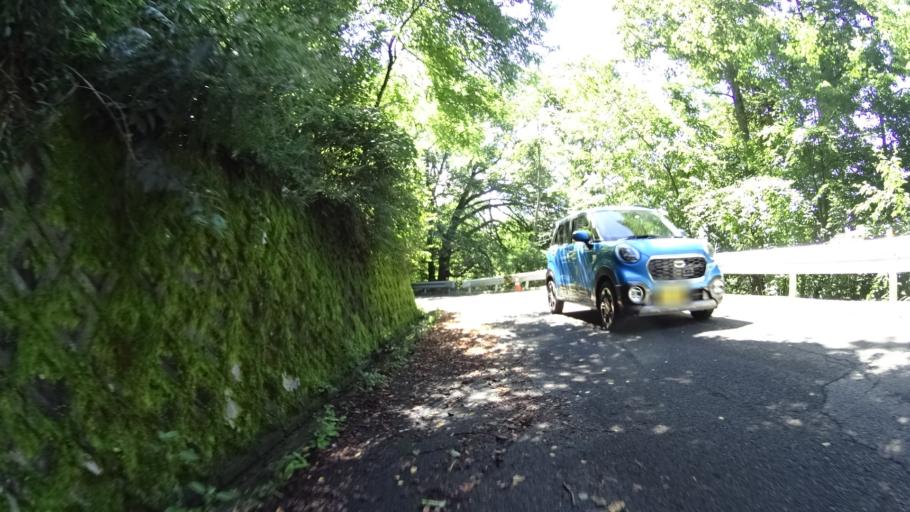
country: JP
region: Yamanashi
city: Enzan
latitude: 35.7372
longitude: 138.8286
